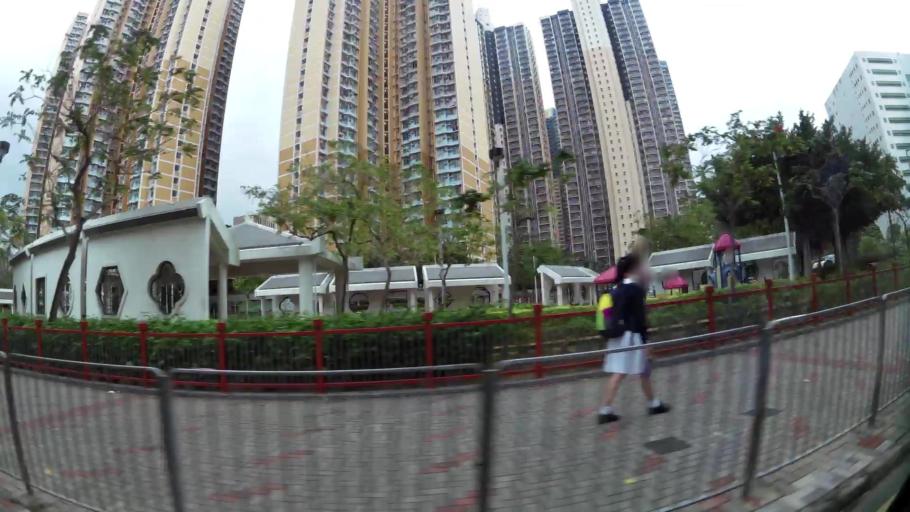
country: HK
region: Tsuen Wan
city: Tsuen Wan
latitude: 22.3677
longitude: 114.1306
